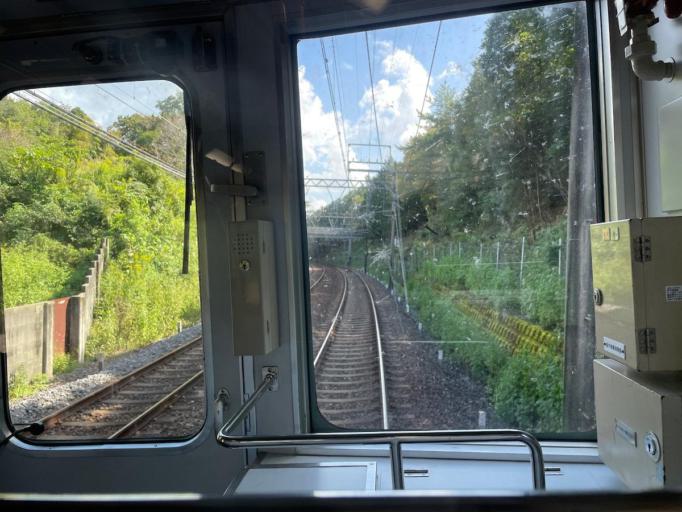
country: JP
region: Mie
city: Ise
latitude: 34.4720
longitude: 136.7392
